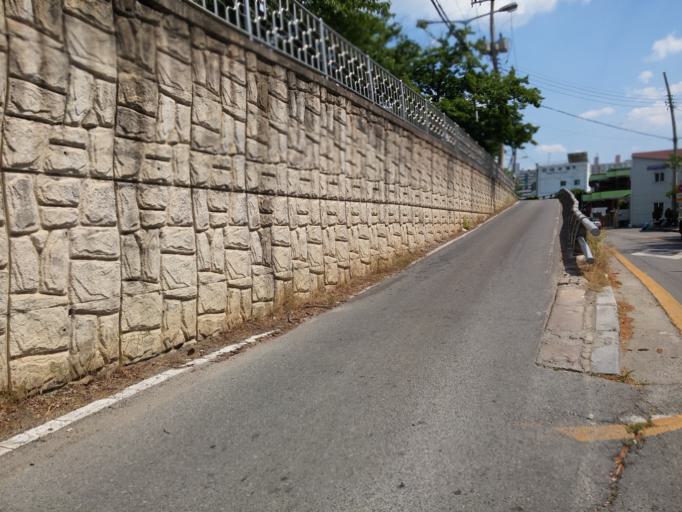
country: KR
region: Chungcheongbuk-do
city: Cheongju-si
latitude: 36.6179
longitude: 127.4923
